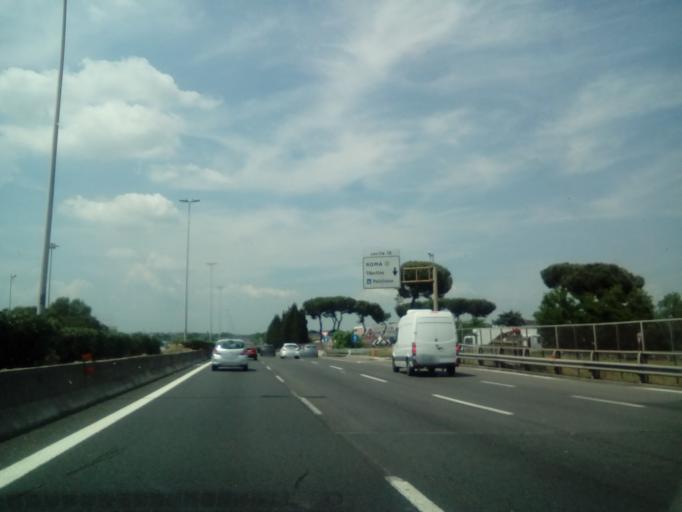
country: IT
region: Latium
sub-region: Citta metropolitana di Roma Capitale
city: Colle Verde
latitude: 41.9331
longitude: 12.6015
